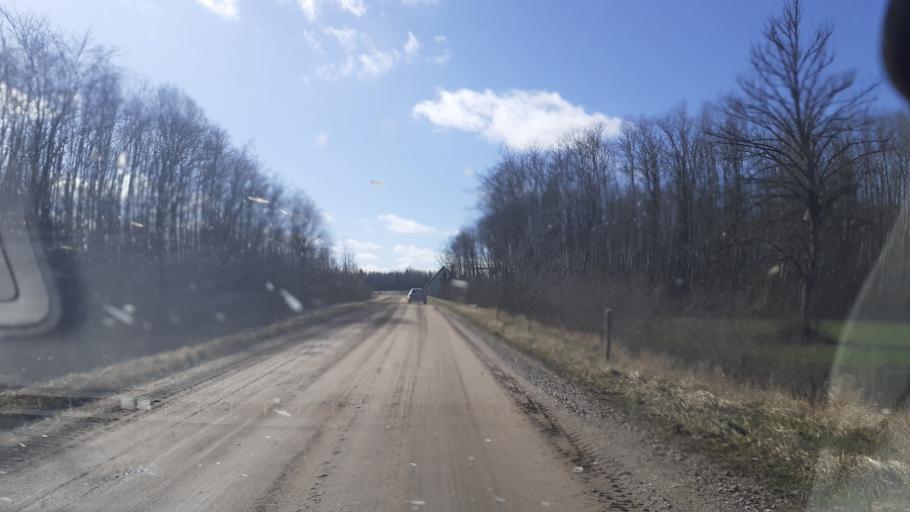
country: LV
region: Kuldigas Rajons
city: Kuldiga
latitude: 56.9234
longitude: 22.1364
